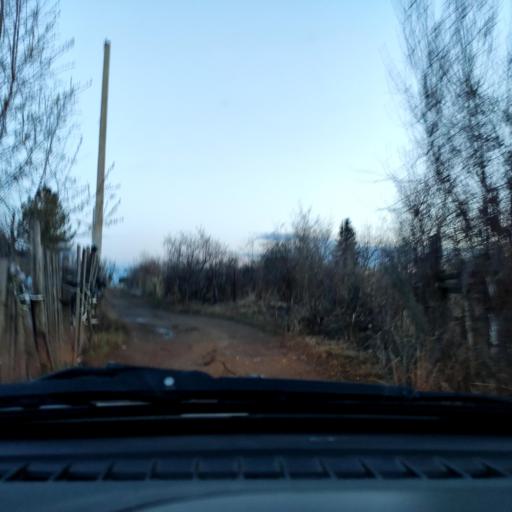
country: RU
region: Perm
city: Froly
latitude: 57.9413
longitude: 56.1975
